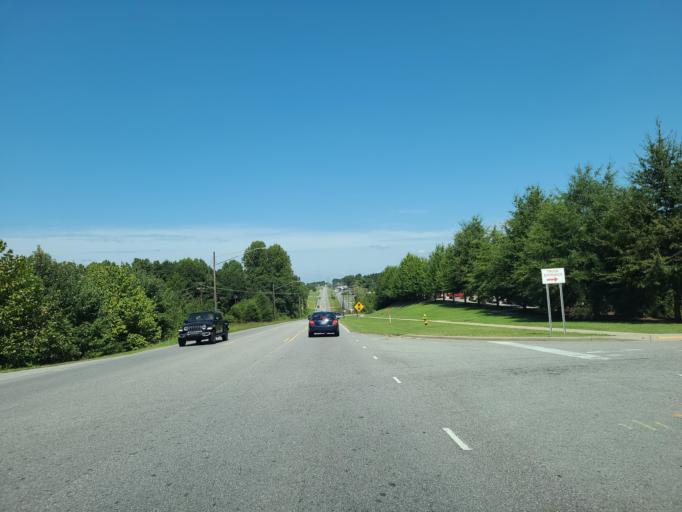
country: US
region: North Carolina
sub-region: Lincoln County
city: Lincolnton
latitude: 35.4825
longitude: -81.2423
